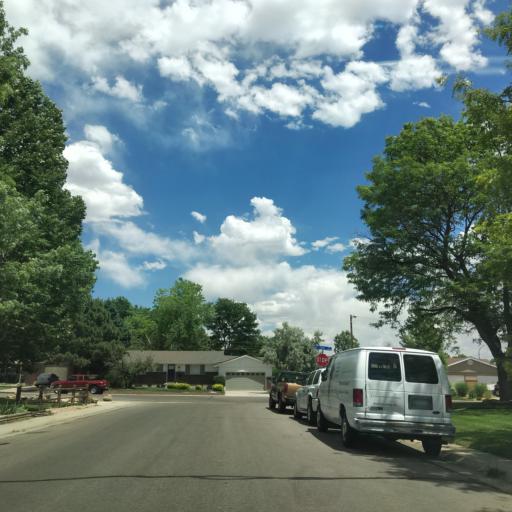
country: US
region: Colorado
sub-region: Jefferson County
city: Lakewood
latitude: 39.6828
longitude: -105.0924
